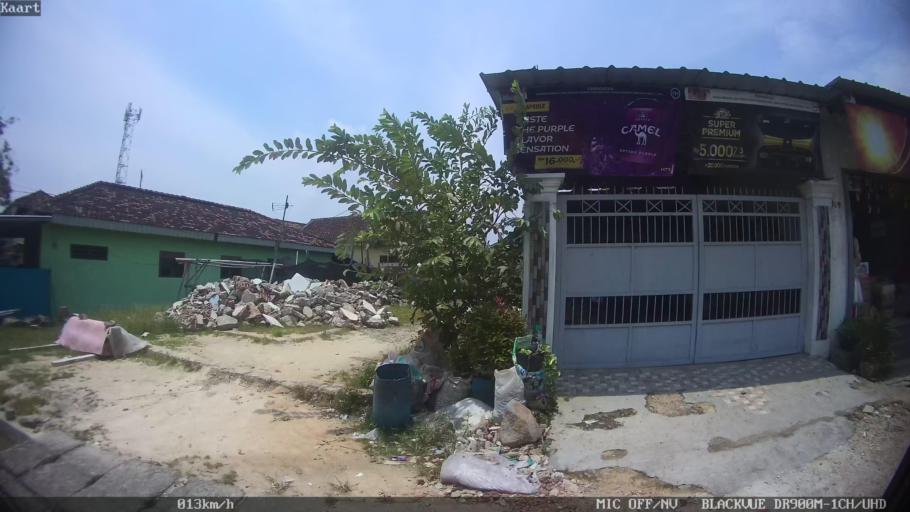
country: ID
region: Lampung
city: Bandarlampung
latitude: -5.4548
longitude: 105.2623
